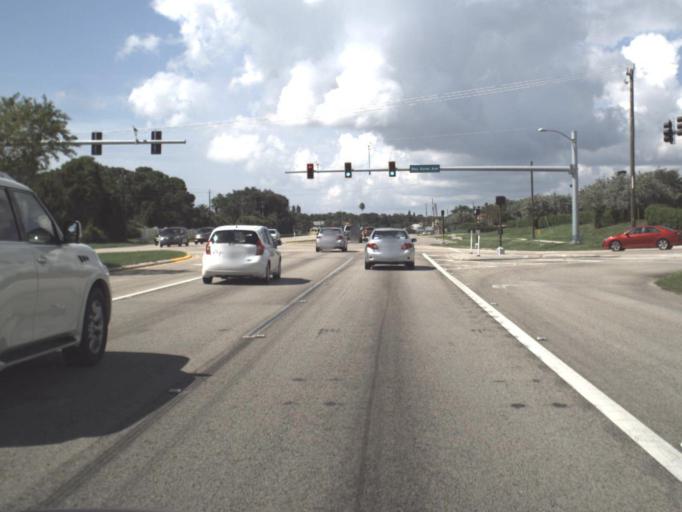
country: US
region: Florida
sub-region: Sarasota County
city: Osprey
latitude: 27.1913
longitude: -82.4881
